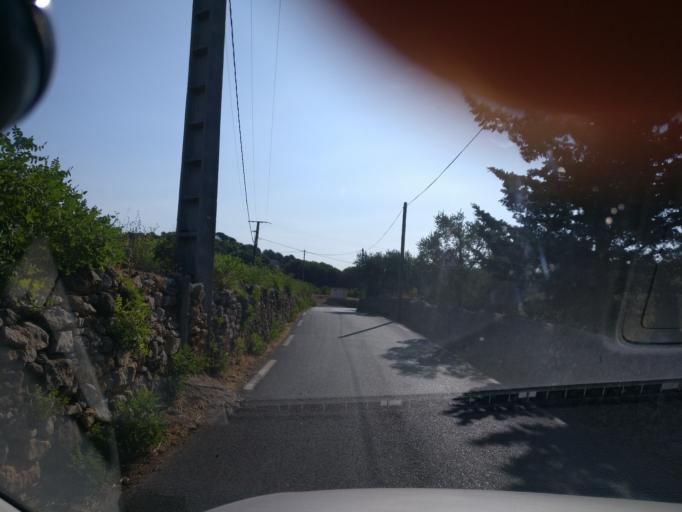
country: FR
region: Provence-Alpes-Cote d'Azur
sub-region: Departement du Var
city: Ollioules
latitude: 43.1348
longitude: 5.8288
